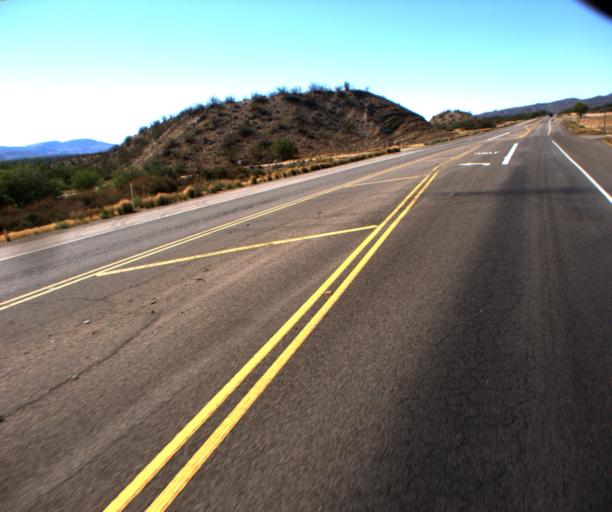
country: US
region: Arizona
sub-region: Yavapai County
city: Bagdad
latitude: 34.7406
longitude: -113.6156
